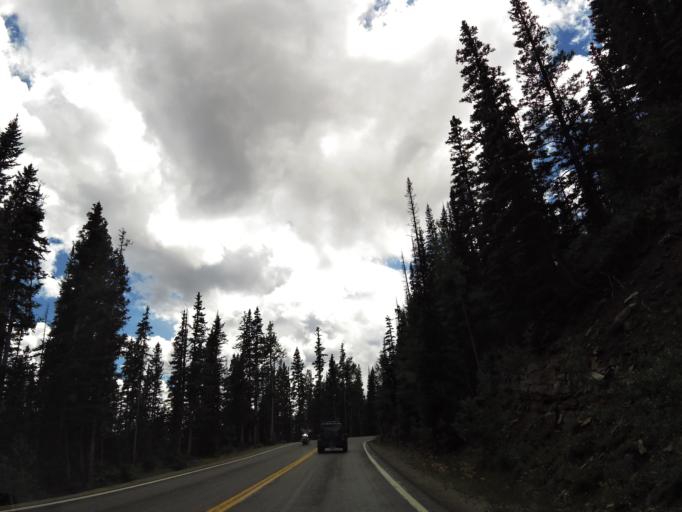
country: US
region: Colorado
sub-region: San Juan County
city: Silverton
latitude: 37.7704
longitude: -107.6711
